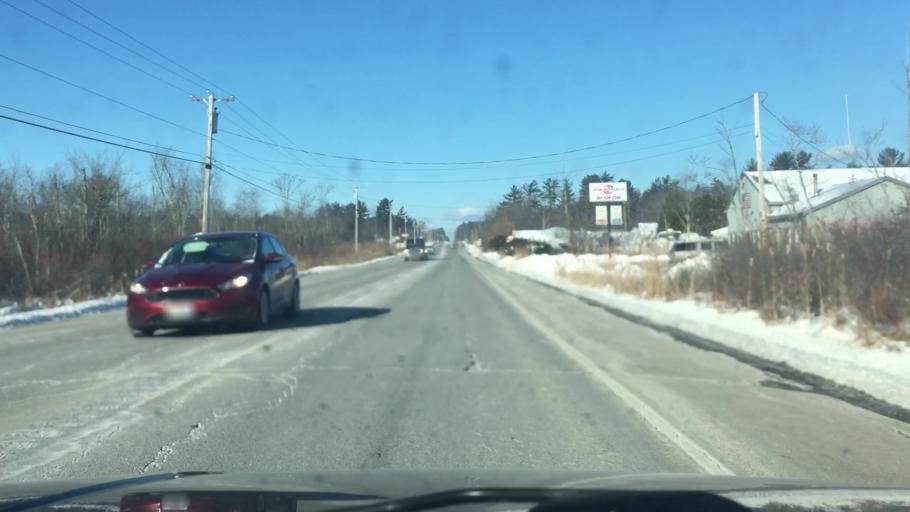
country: US
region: Maine
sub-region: York County
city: South Eliot
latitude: 43.1262
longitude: -70.7664
